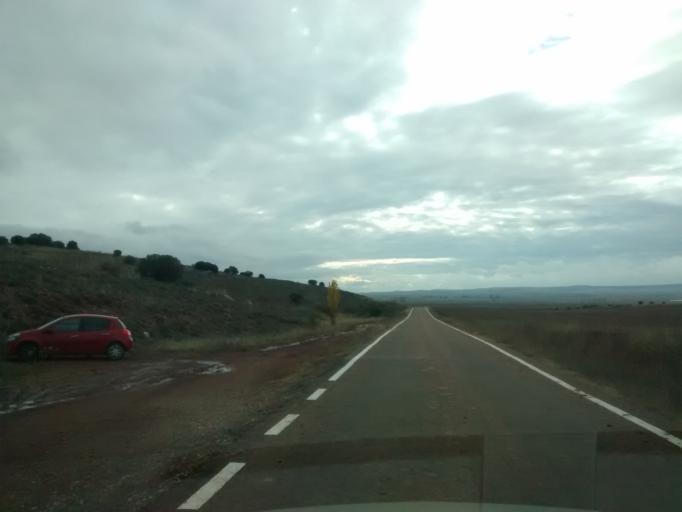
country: ES
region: Aragon
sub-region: Provincia de Teruel
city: Tornos
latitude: 40.9784
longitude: -1.4650
